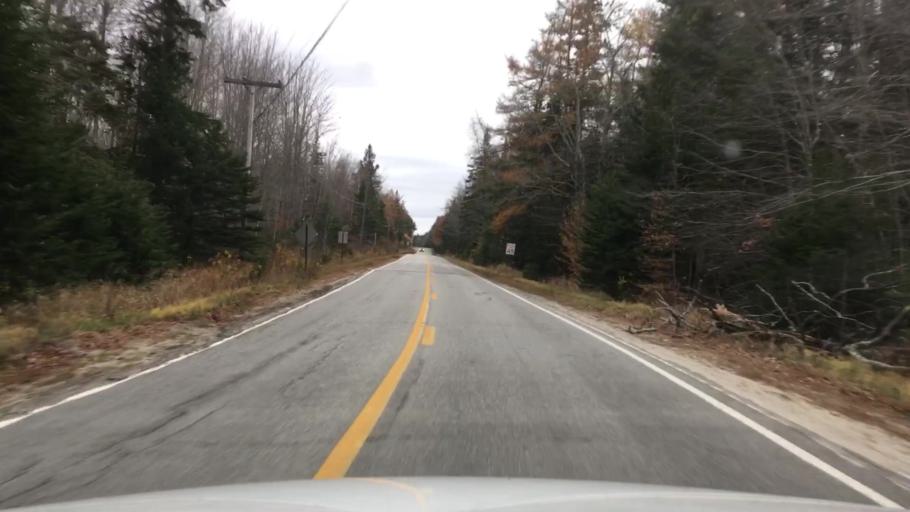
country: US
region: Maine
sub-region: Hancock County
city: Sedgwick
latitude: 44.2784
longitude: -68.5535
